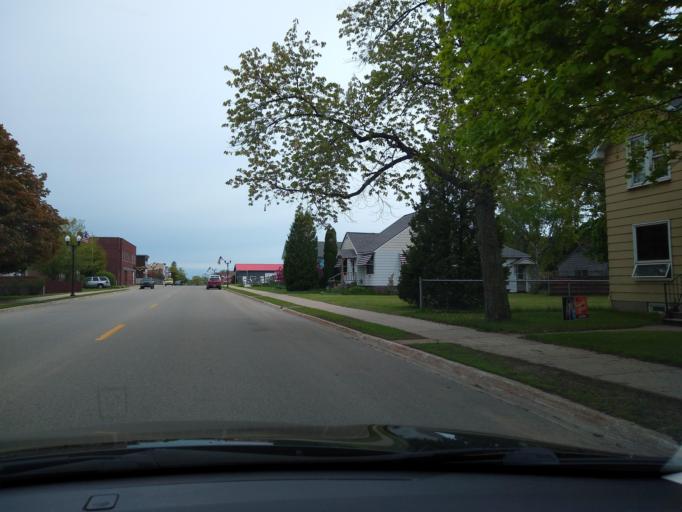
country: US
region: Michigan
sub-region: Delta County
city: Escanaba
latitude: 45.7635
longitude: -87.0691
